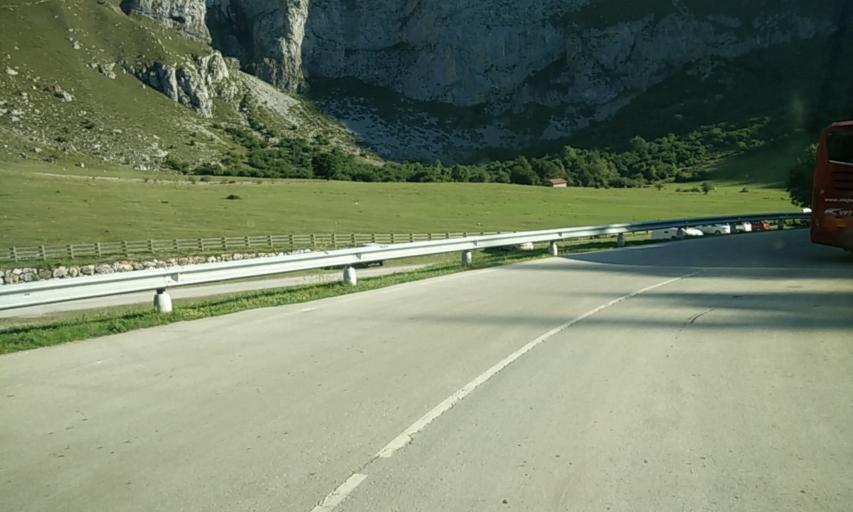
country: ES
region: Castille and Leon
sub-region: Provincia de Leon
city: Posada de Valdeon
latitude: 43.1442
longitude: -4.8133
